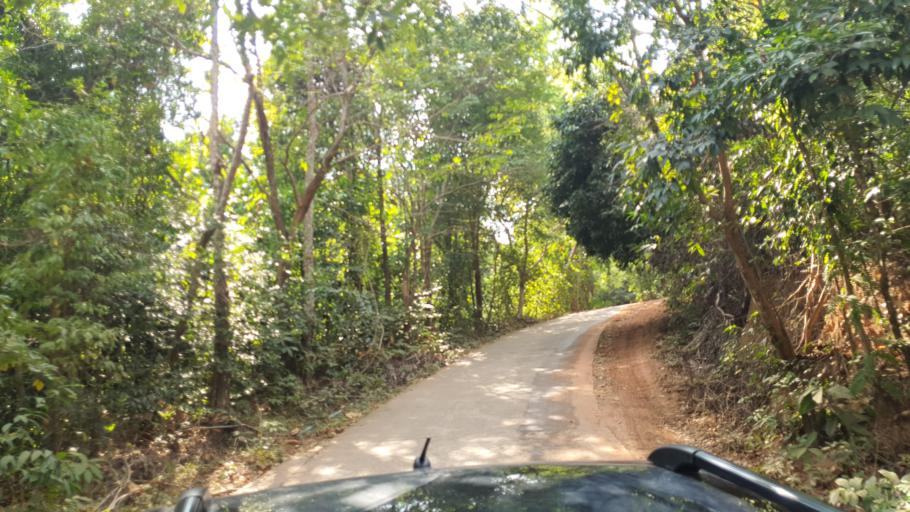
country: TH
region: Changwat Bueng Kan
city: Si Wilai
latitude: 18.2715
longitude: 103.7971
